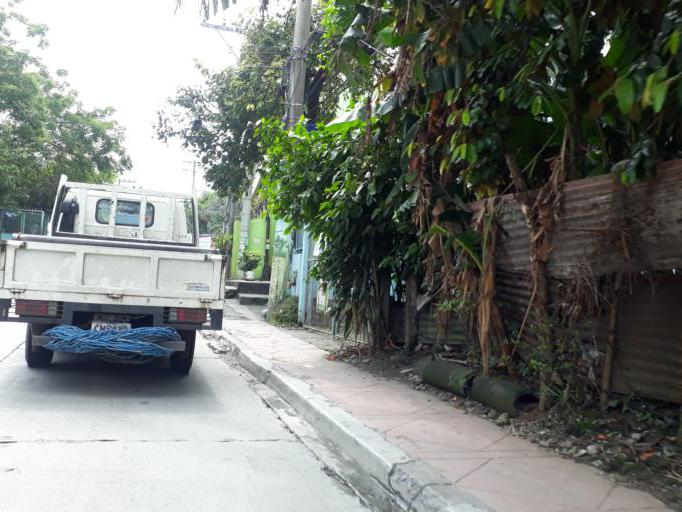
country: PH
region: Calabarzon
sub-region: Province of Rizal
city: Valenzuela
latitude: 14.7043
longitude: 121.0043
